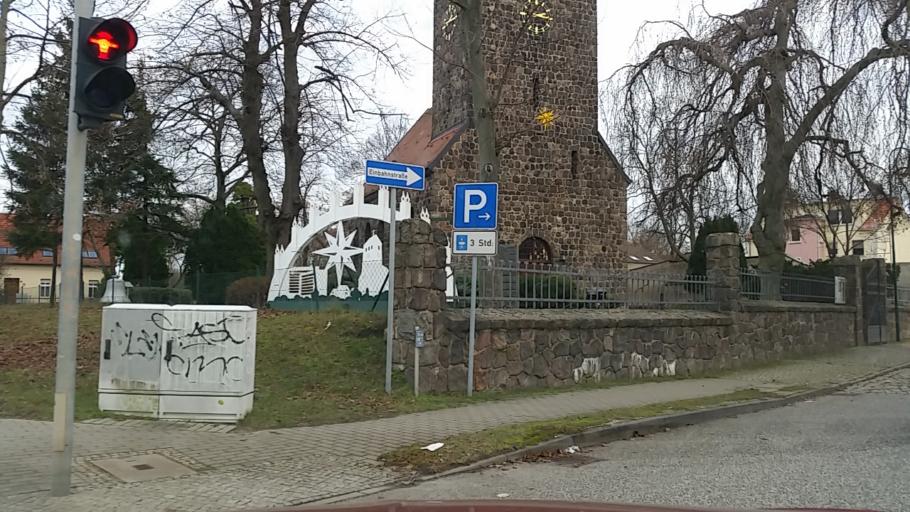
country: DE
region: Brandenburg
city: Schonefeld
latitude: 52.3872
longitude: 13.5057
